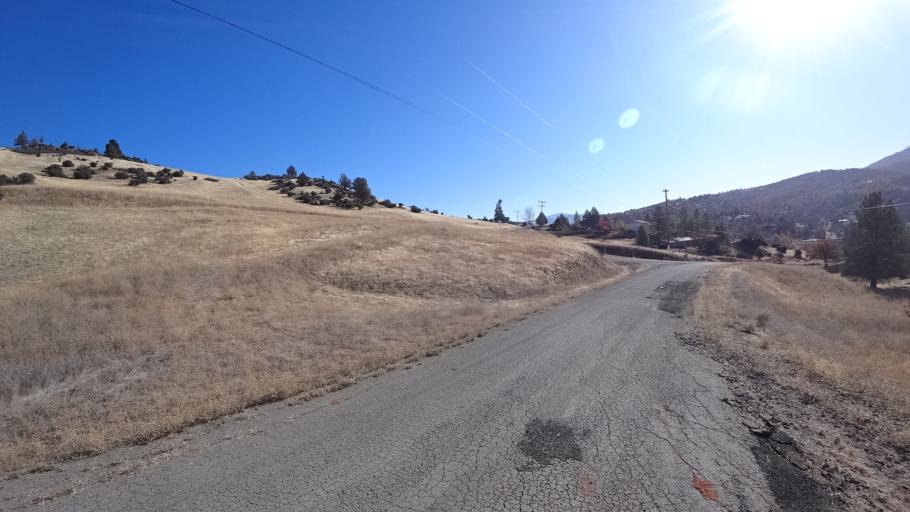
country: US
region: California
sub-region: Siskiyou County
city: Montague
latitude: 41.8998
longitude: -122.5234
